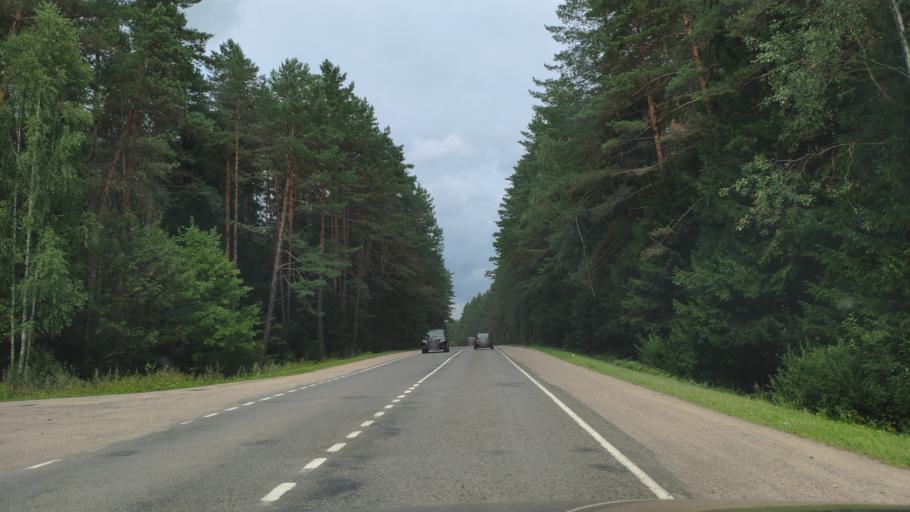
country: BY
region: Minsk
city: Zaslawye
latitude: 53.9781
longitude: 27.2504
